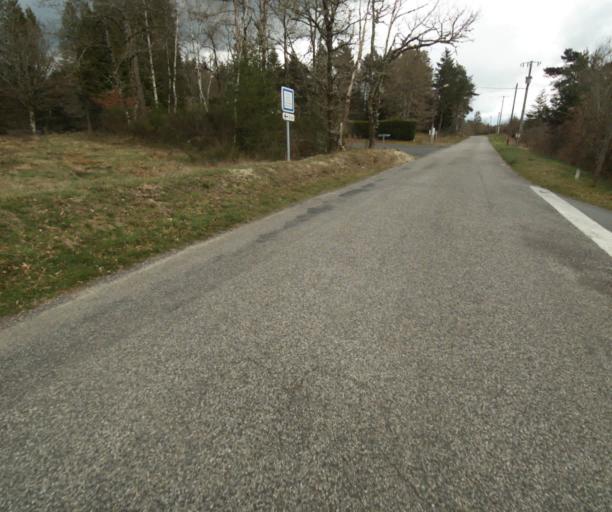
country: FR
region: Limousin
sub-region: Departement de la Correze
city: Correze
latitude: 45.2894
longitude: 1.9669
